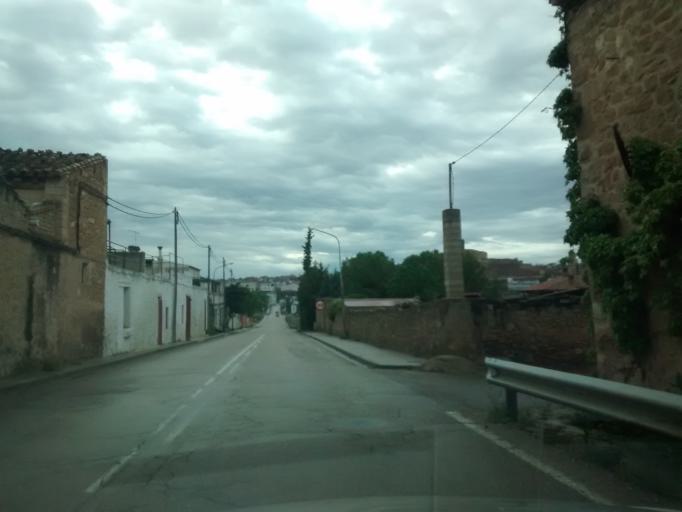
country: ES
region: Aragon
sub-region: Provincia de Zaragoza
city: Maella
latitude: 41.1173
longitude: 0.1458
